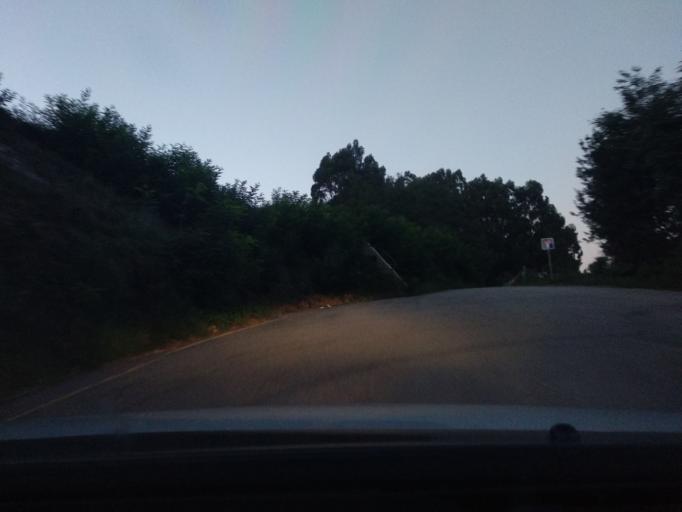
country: ES
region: Galicia
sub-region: Provincia de Pontevedra
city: Moana
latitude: 42.2882
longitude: -8.7530
